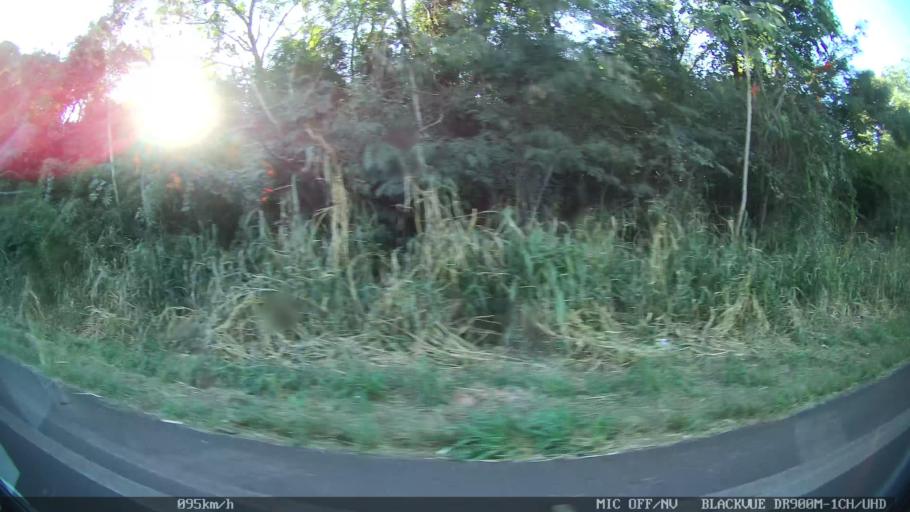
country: BR
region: Sao Paulo
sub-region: Guapiacu
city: Guapiacu
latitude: -20.7571
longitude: -49.1618
